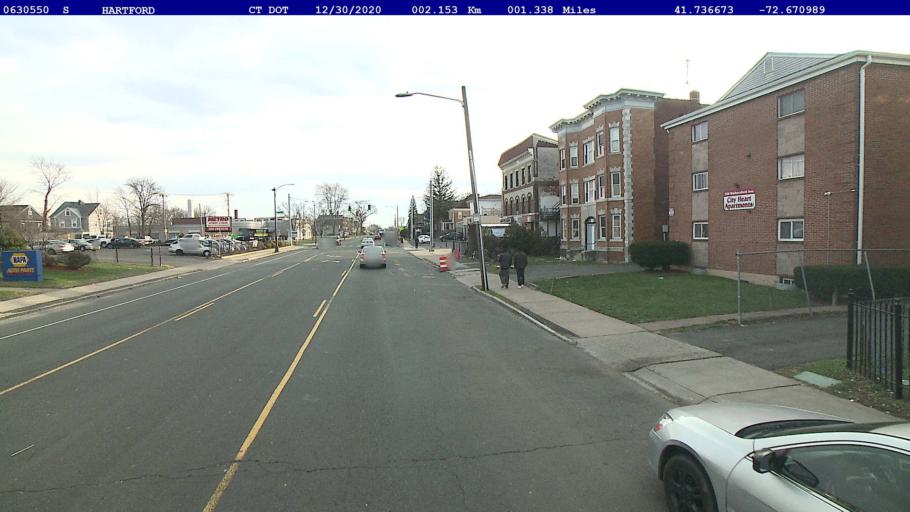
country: US
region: Connecticut
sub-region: Hartford County
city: Wethersfield
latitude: 41.7367
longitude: -72.6710
